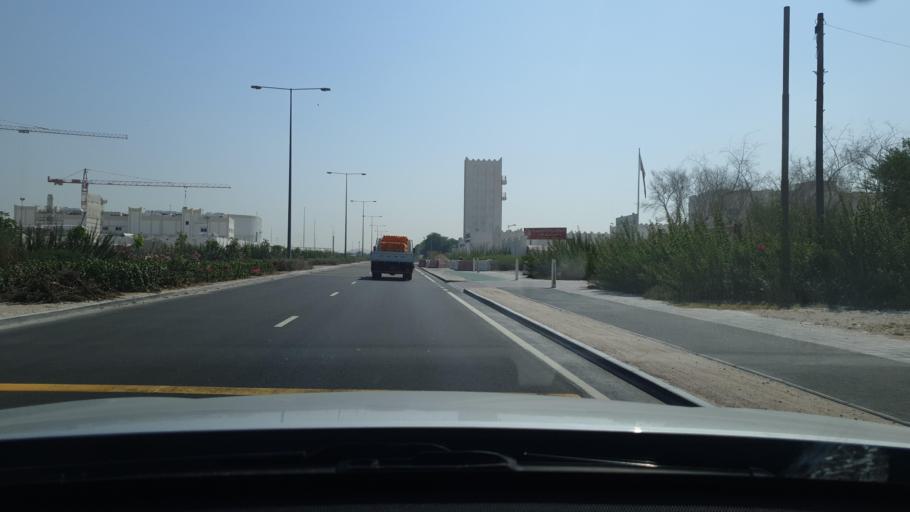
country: QA
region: Baladiyat ad Dawhah
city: Doha
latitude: 25.2331
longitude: 51.5212
